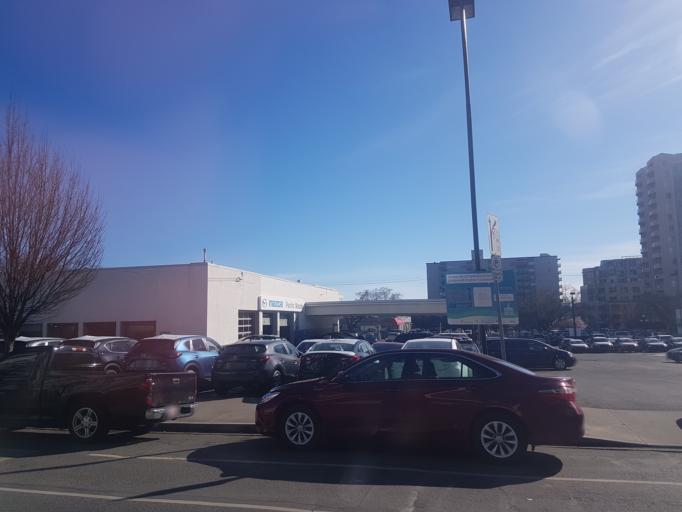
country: CA
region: British Columbia
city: Victoria
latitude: 48.4260
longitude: -123.3544
